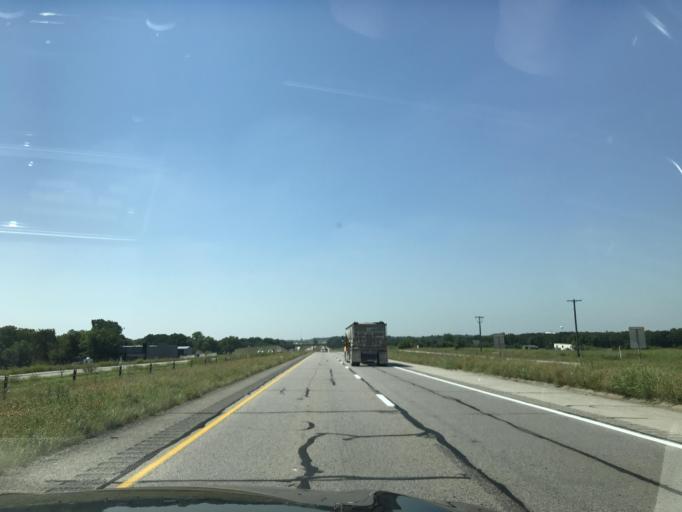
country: US
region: Texas
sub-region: Johnson County
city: Grandview
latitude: 32.3035
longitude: -97.1817
